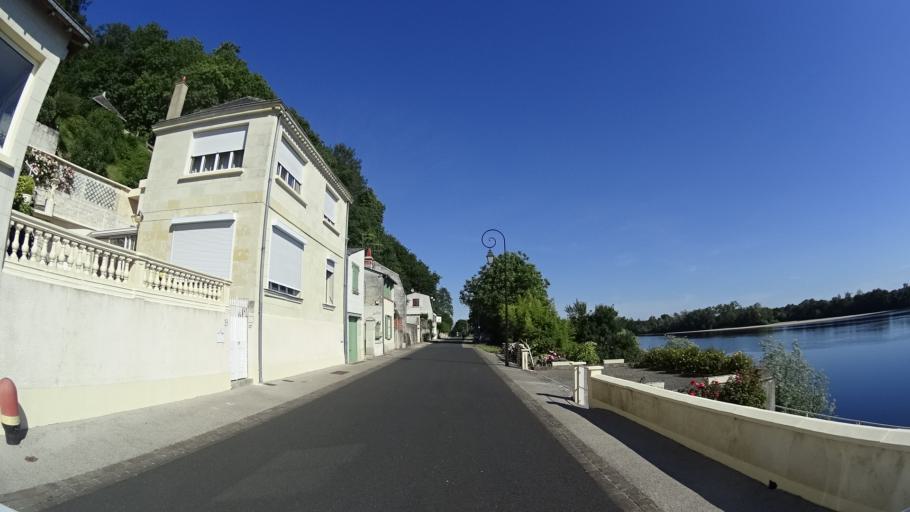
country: FR
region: Pays de la Loire
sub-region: Departement de Maine-et-Loire
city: Saint-Martin-de-la-Place
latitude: 47.3004
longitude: -0.1425
